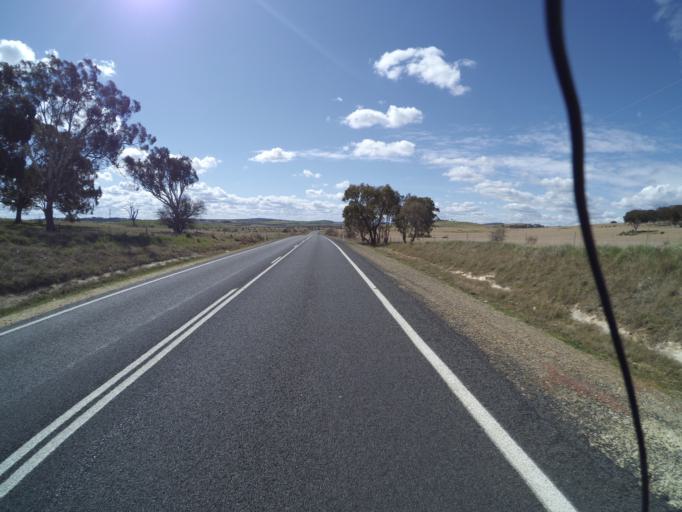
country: AU
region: New South Wales
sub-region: Goulburn Mulwaree
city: Goulburn
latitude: -34.8146
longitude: 149.6845
